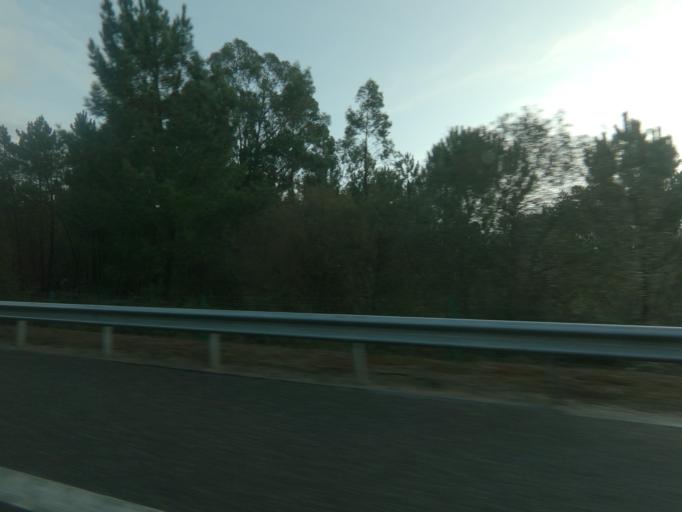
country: ES
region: Galicia
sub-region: Provincia de Pontevedra
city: Tui
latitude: 42.0998
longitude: -8.6438
